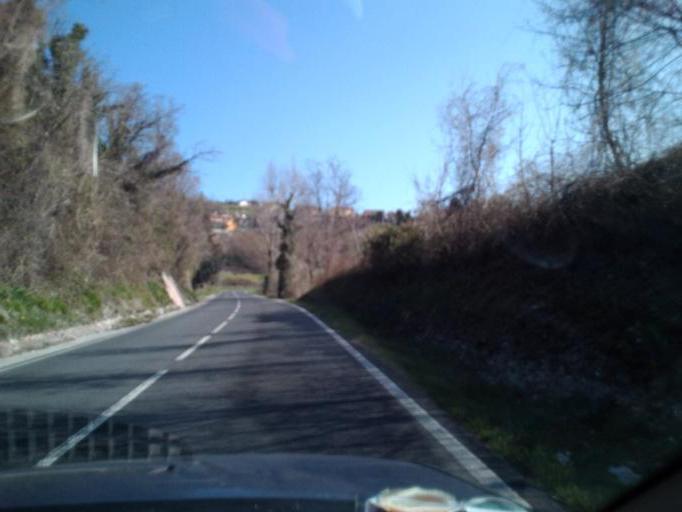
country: IT
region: Veneto
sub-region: Provincia di Verona
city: Grezzana
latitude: 45.5490
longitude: 11.0240
